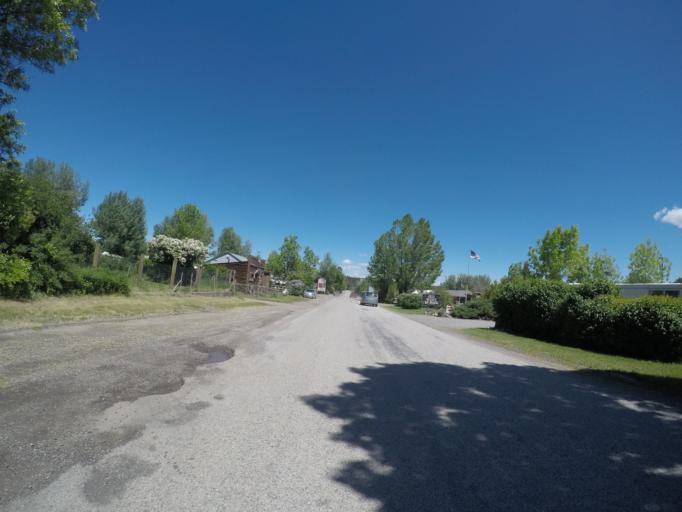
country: US
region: Montana
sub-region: Stillwater County
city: Absarokee
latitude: 45.7060
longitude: -109.5419
